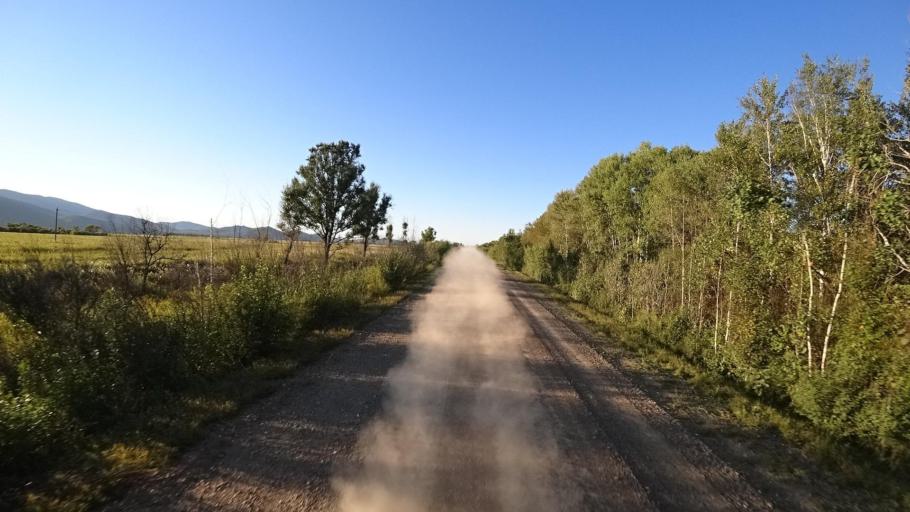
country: RU
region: Primorskiy
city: Kirovskiy
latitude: 44.7921
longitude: 133.6226
